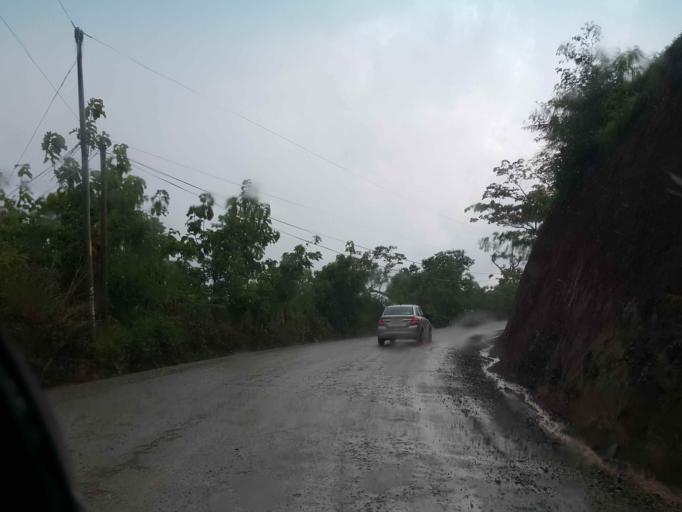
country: CR
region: Guanacaste
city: Juntas
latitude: 10.2277
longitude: -84.8522
